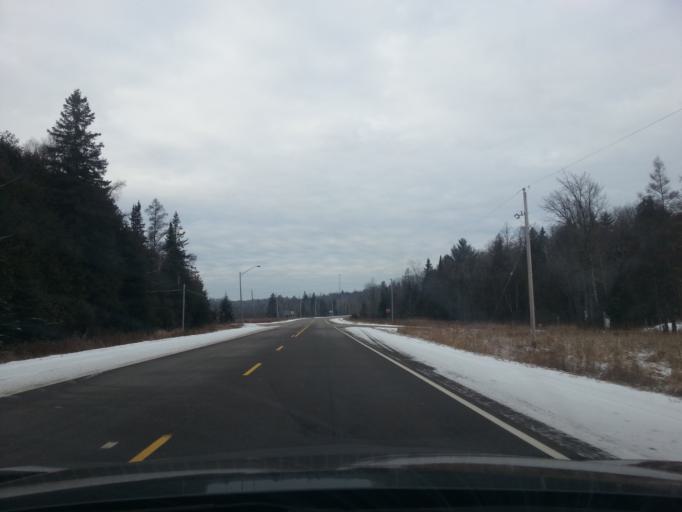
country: CA
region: Ontario
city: Skatepark
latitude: 44.7529
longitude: -76.8262
